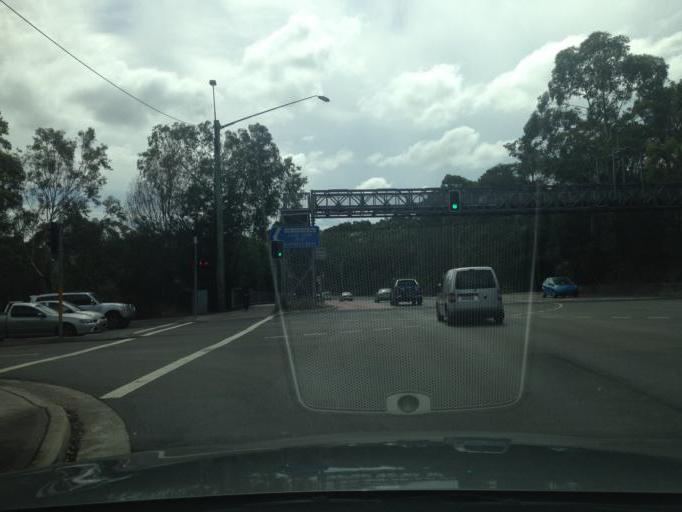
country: AU
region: New South Wales
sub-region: Lane Cove
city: Lane Cove West
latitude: -33.8066
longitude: 151.1536
